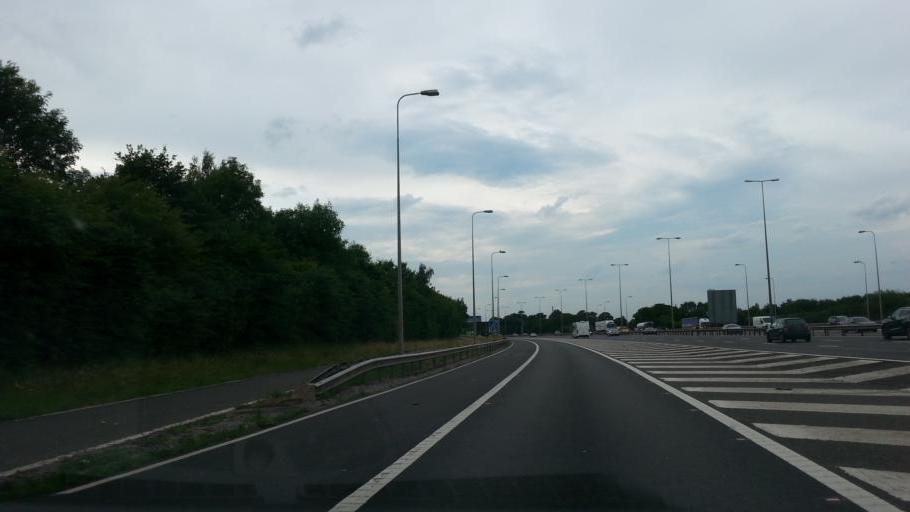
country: GB
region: England
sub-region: Worcestershire
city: Bredon
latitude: 52.0540
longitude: -2.1395
